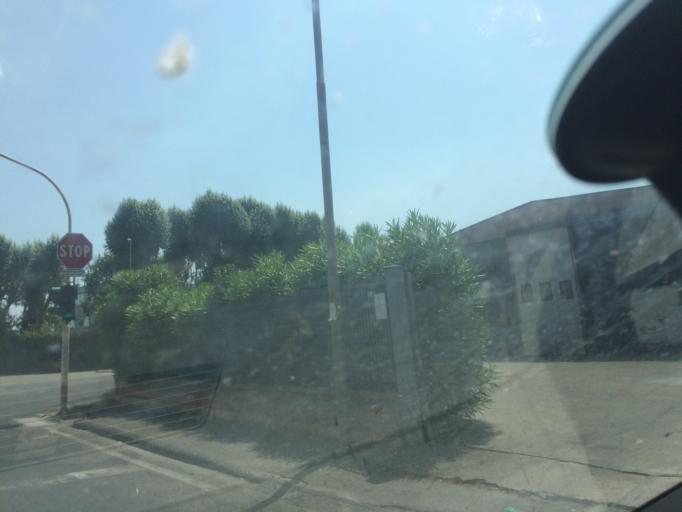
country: IT
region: Tuscany
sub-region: Provincia di Massa-Carrara
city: Carrara
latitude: 44.0434
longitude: 10.0636
